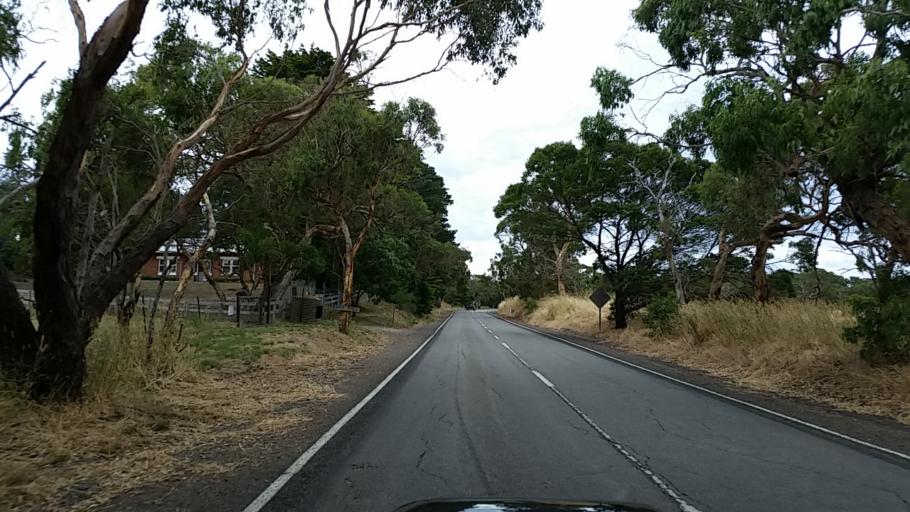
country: AU
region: South Australia
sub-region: Onkaparinga
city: Aldinga
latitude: -35.3768
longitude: 138.4643
